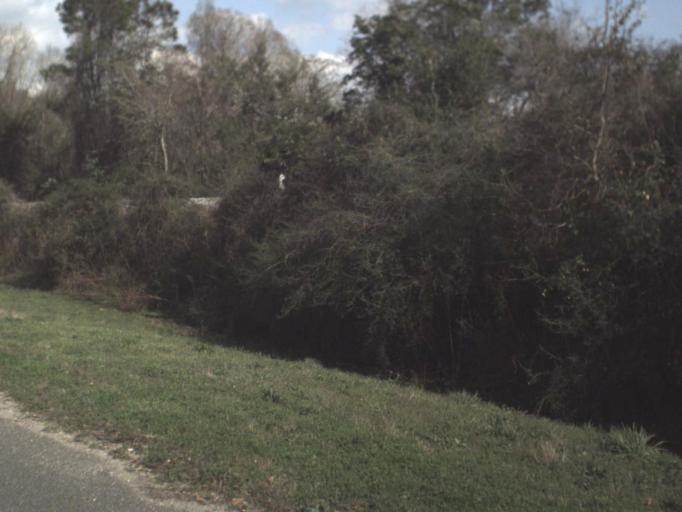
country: US
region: Florida
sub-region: Bay County
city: Hiland Park
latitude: 30.2578
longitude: -85.5442
